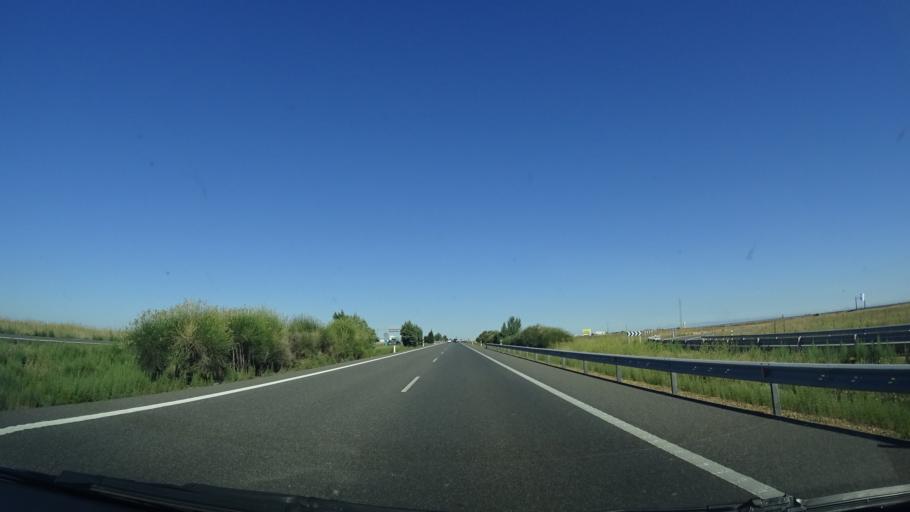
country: ES
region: Castille and Leon
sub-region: Provincia de Zamora
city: Castrogonzalo
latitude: 41.9690
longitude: -5.5961
